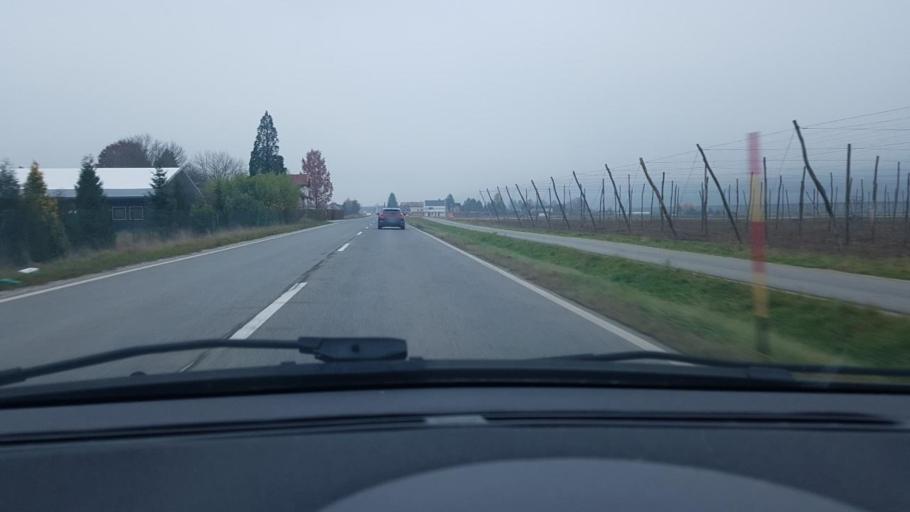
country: SI
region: Zalec
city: Zalec
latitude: 46.2436
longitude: 15.2067
